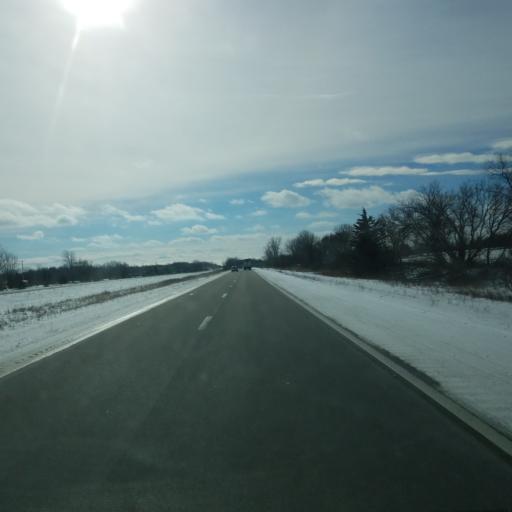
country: US
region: Michigan
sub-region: Gratiot County
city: Ithaca
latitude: 43.3452
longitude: -84.6018
